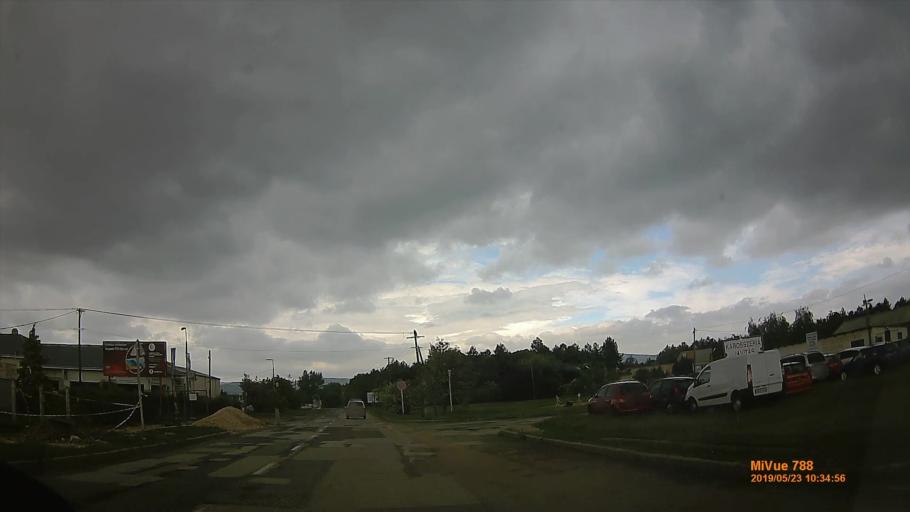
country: HU
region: Veszprem
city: Veszprem
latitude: 47.1067
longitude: 17.8946
